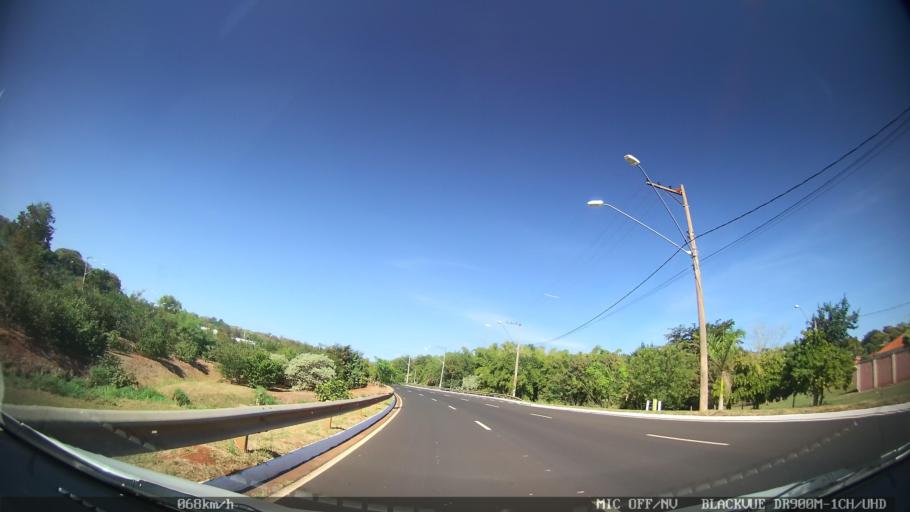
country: BR
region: Sao Paulo
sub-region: Ribeirao Preto
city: Ribeirao Preto
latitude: -21.2374
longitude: -47.7642
